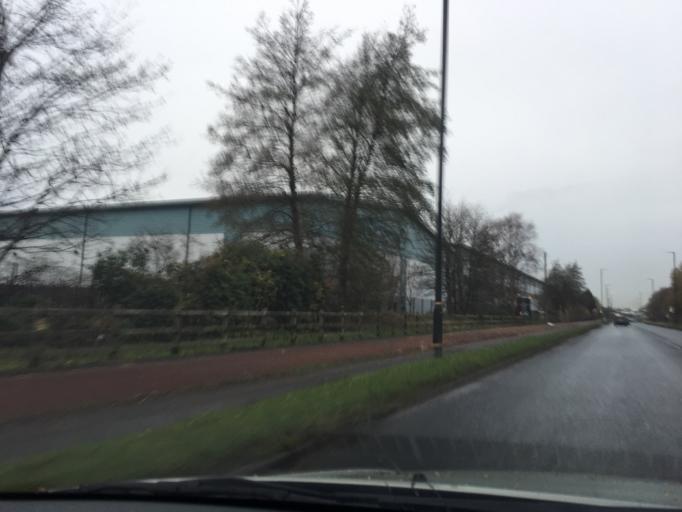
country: GB
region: England
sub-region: Trafford
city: Stretford
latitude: 53.4577
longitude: -2.3217
